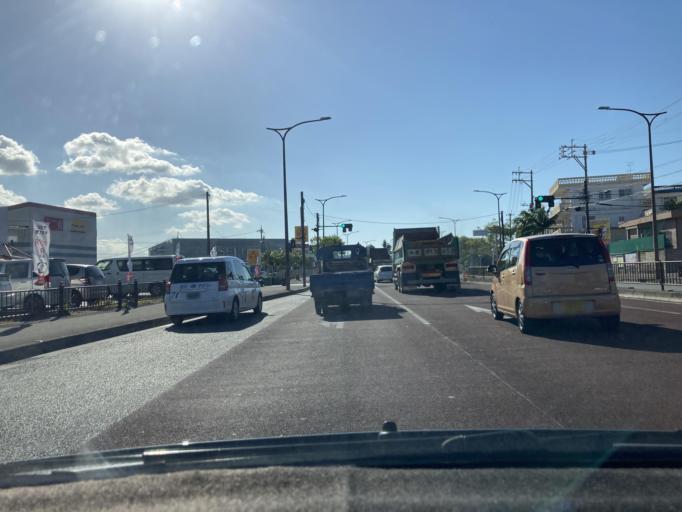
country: JP
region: Okinawa
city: Ishikawa
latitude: 26.4341
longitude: 127.8347
